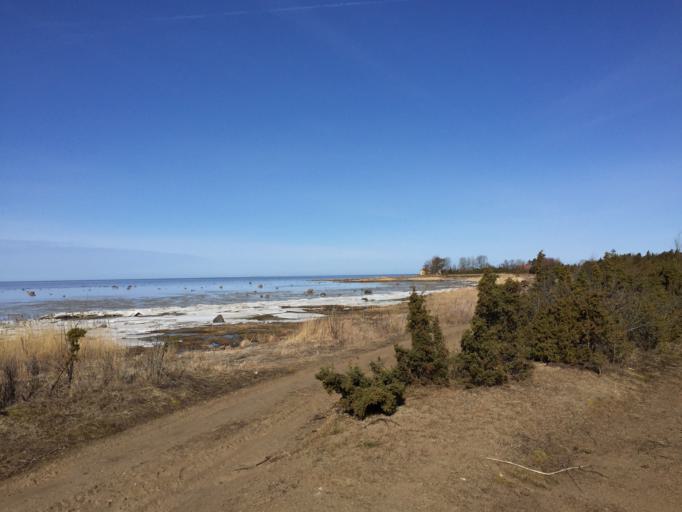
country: EE
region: Laeaene
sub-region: Haapsalu linn
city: Haapsalu
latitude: 58.6507
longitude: 23.5064
